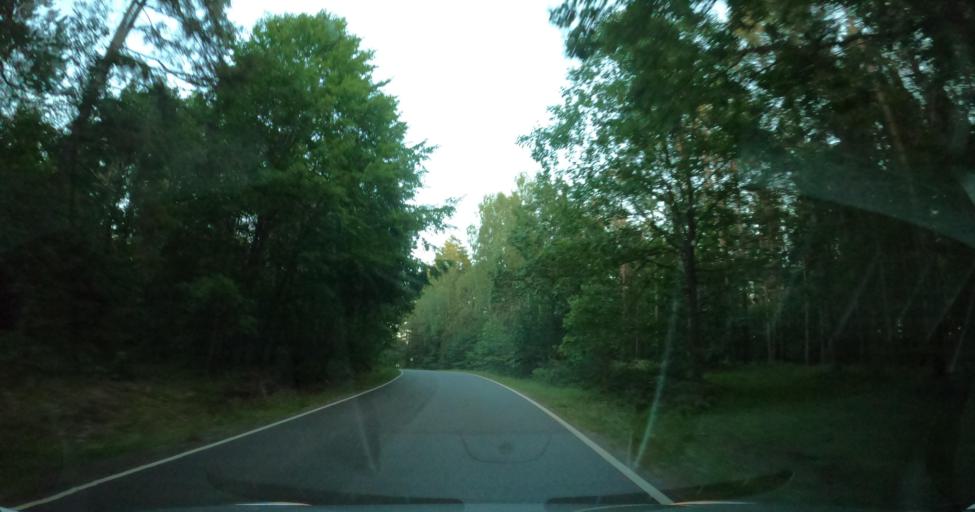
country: PL
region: Pomeranian Voivodeship
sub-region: Powiat leborski
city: Lebork
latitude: 54.4993
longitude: 17.8359
